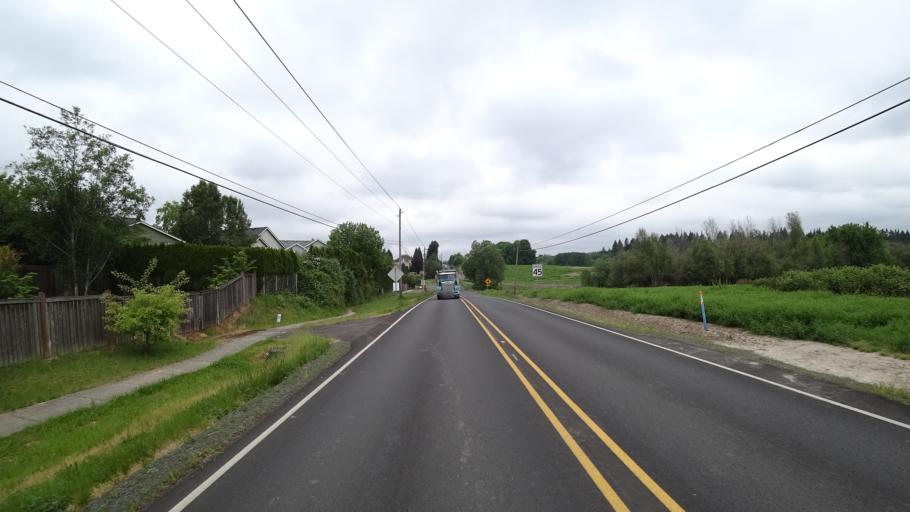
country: US
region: Oregon
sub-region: Washington County
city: Rockcreek
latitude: 45.5616
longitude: -122.8855
